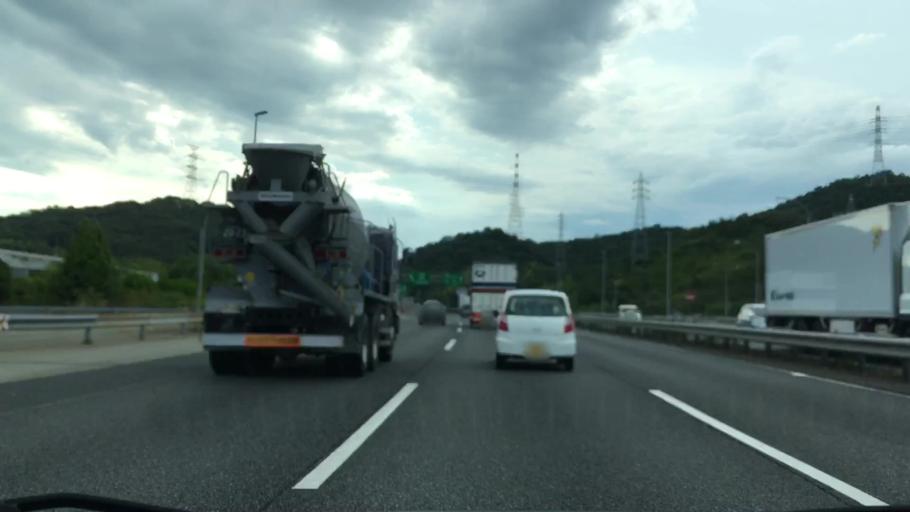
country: JP
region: Hyogo
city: Shirahamacho-usazakiminami
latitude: 34.8002
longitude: 134.7452
